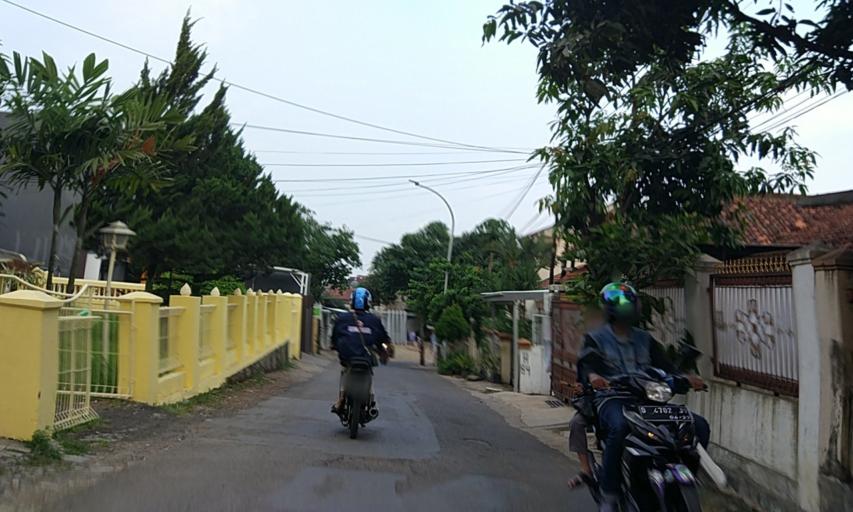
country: ID
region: West Java
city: Bandung
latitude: -6.9119
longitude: 107.6810
